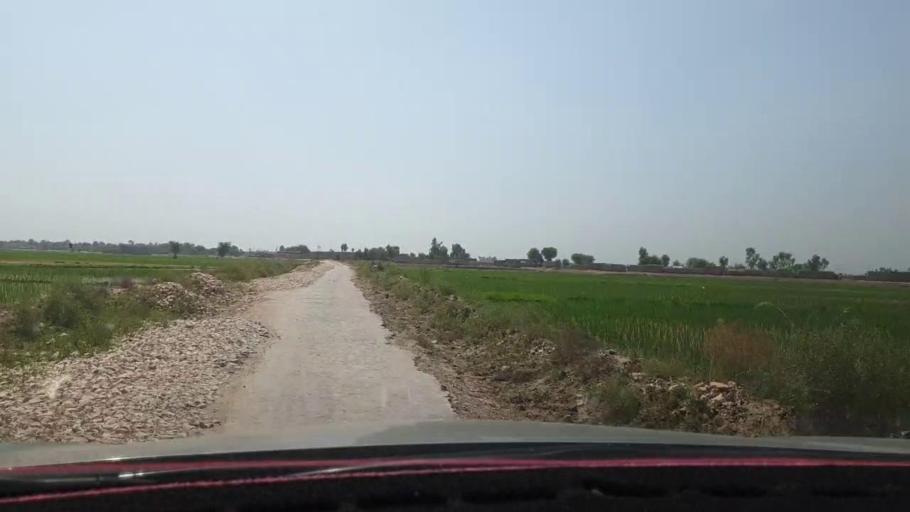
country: PK
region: Sindh
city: Warah
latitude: 27.4889
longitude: 67.8203
